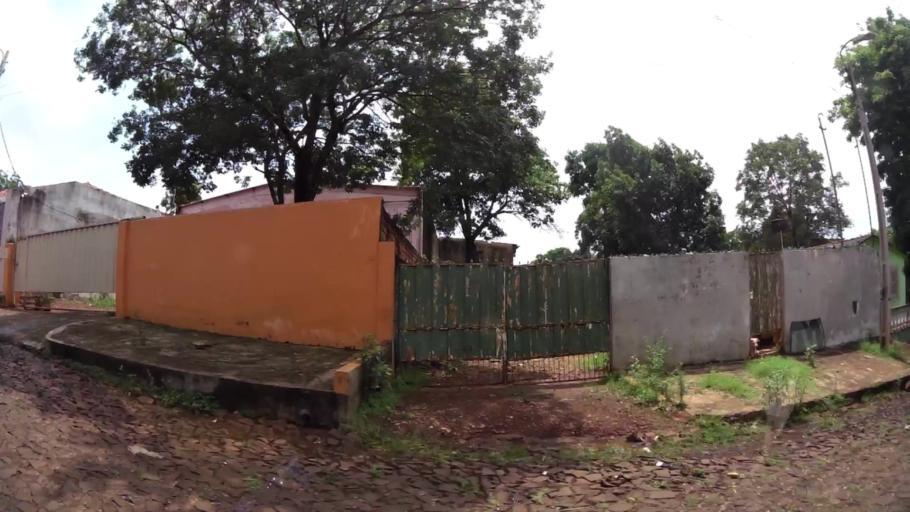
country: PY
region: Alto Parana
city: Ciudad del Este
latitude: -25.5082
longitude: -54.6595
